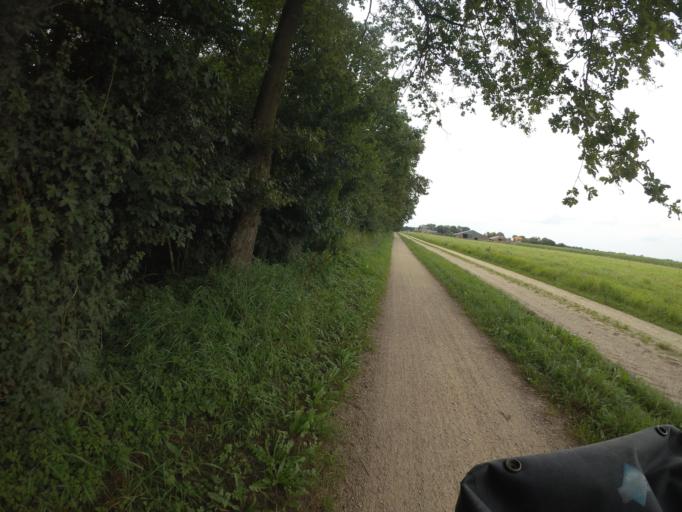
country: NL
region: Limburg
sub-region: Gemeente Gennep
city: Gennep
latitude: 51.6589
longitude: 6.0258
